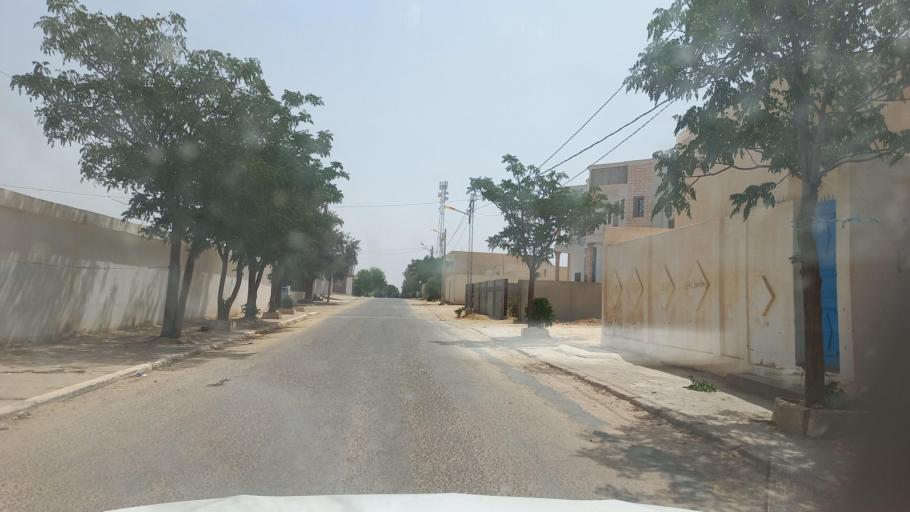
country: TN
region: Al Qasrayn
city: Kasserine
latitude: 35.2549
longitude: 9.0226
